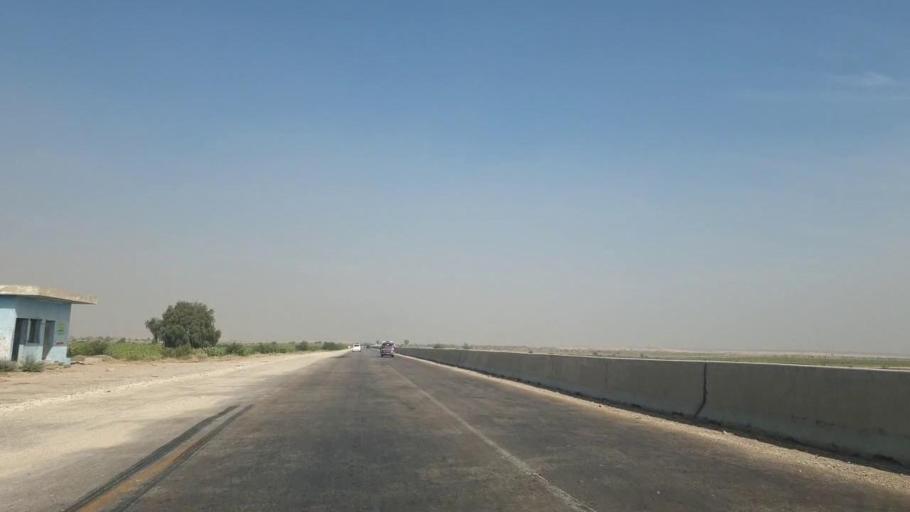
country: PK
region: Sindh
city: Jamshoro
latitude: 25.5387
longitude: 68.2872
